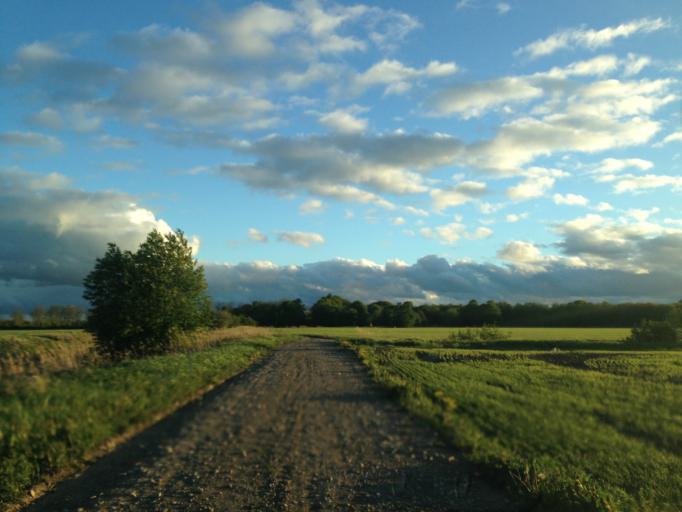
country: EE
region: Raplamaa
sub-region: Maerjamaa vald
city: Marjamaa
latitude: 58.7452
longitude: 24.1686
